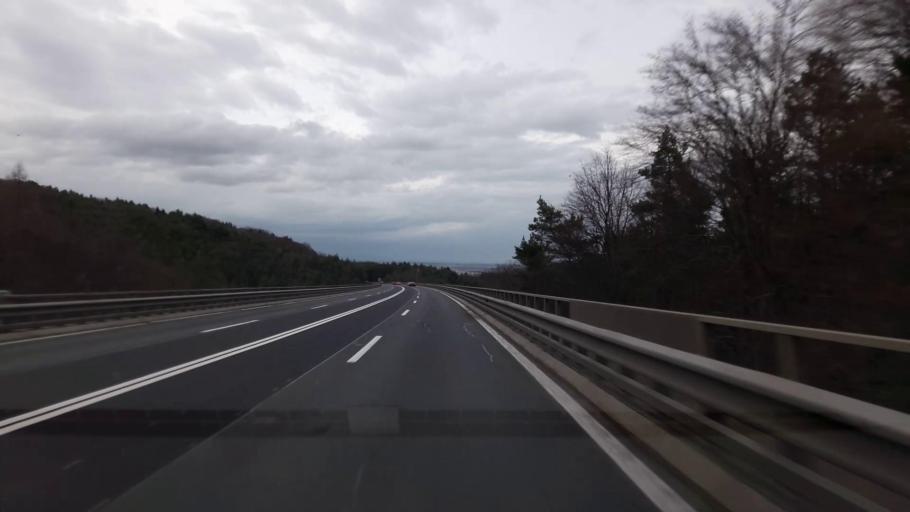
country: AT
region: Burgenland
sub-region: Politischer Bezirk Mattersburg
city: Sieggraben
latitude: 47.6829
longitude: 16.3838
